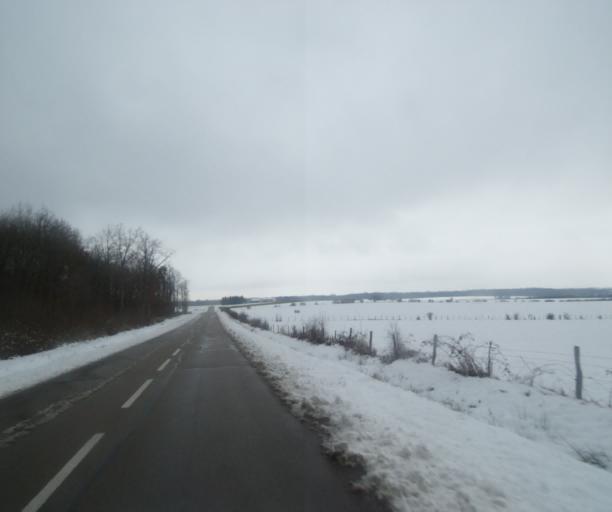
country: FR
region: Champagne-Ardenne
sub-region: Departement de la Haute-Marne
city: Laneuville-a-Remy
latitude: 48.4396
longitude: 4.8577
